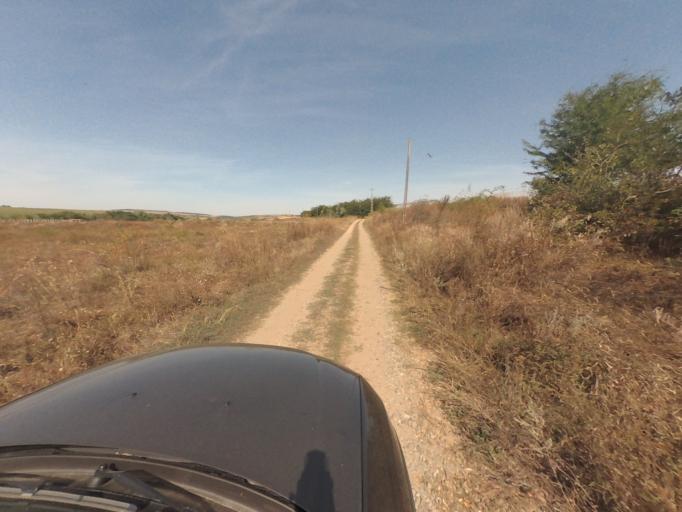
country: RO
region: Vaslui
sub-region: Comuna Costesti
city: Costesti
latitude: 46.5231
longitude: 27.7391
